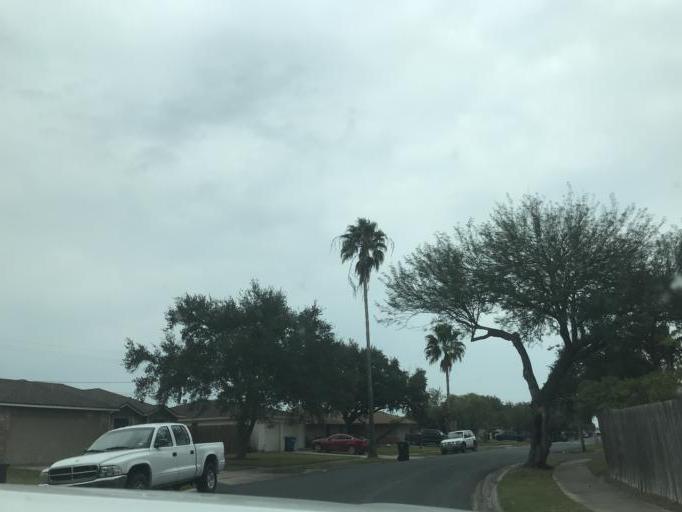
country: US
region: Texas
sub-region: Nueces County
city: Corpus Christi
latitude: 27.6730
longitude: -97.3490
